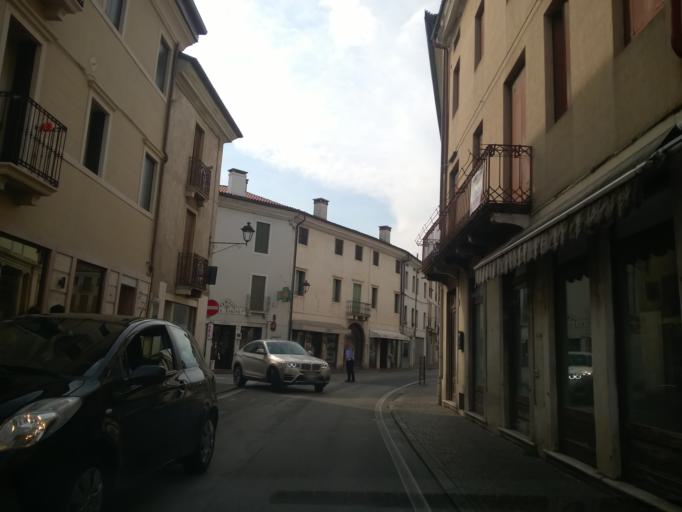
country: IT
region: Veneto
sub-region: Provincia di Vicenza
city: Malo
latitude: 45.6566
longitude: 11.4058
